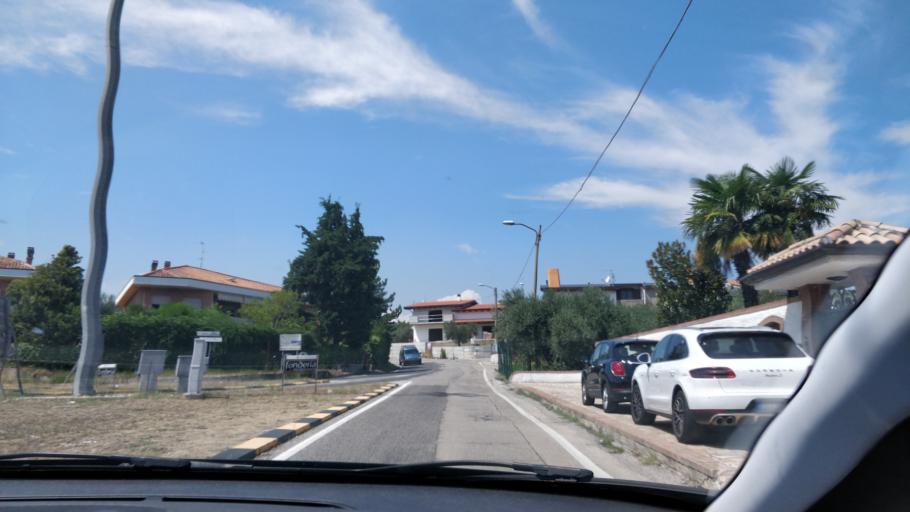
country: IT
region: Abruzzo
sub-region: Provincia di Chieti
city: Francavilla al Mare
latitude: 42.4241
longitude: 14.2702
